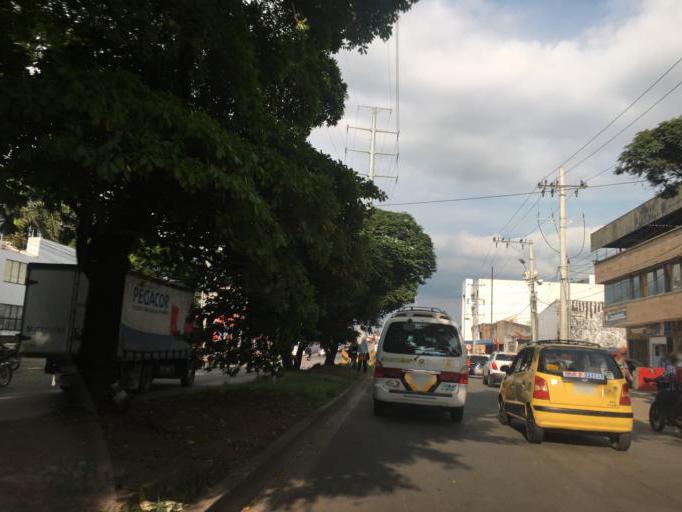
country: CO
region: Valle del Cauca
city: Cali
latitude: 3.4164
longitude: -76.5390
